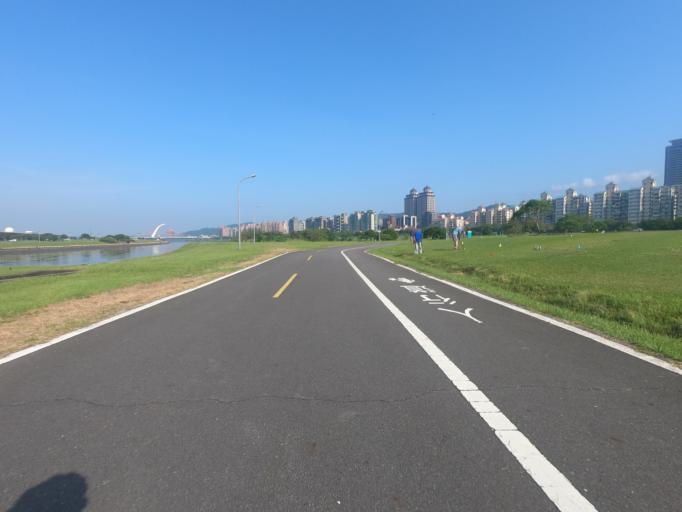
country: TW
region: Taipei
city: Taipei
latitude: 25.0740
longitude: 121.5604
